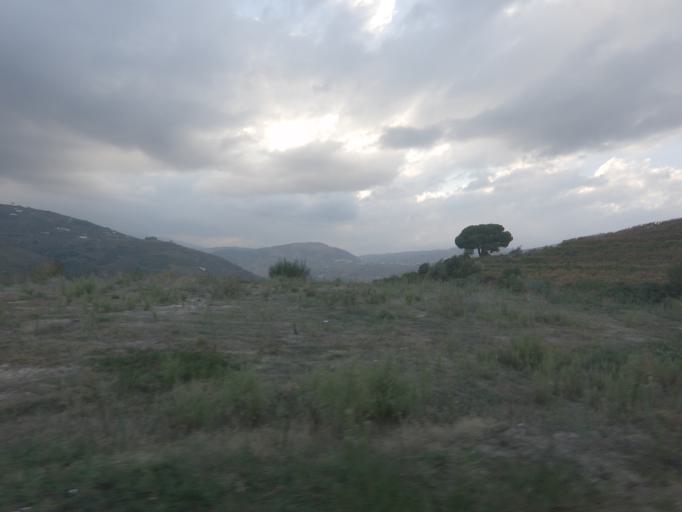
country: PT
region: Vila Real
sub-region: Mesao Frio
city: Mesao Frio
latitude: 41.1618
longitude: -7.8520
